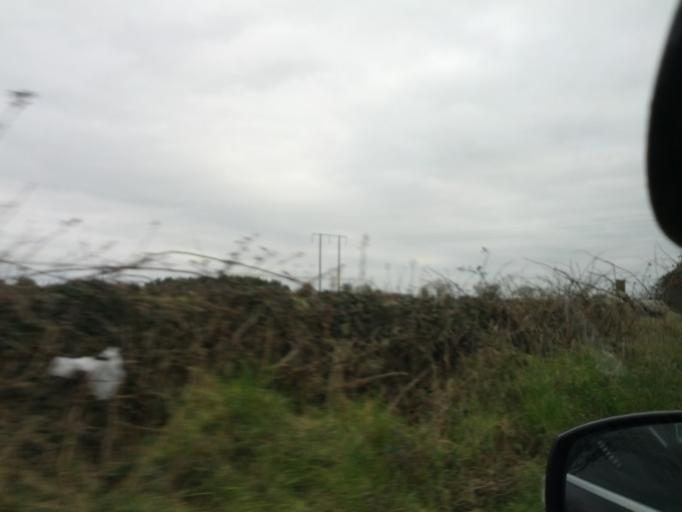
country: IE
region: Connaught
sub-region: County Galway
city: Athenry
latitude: 53.2711
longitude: -8.7434
